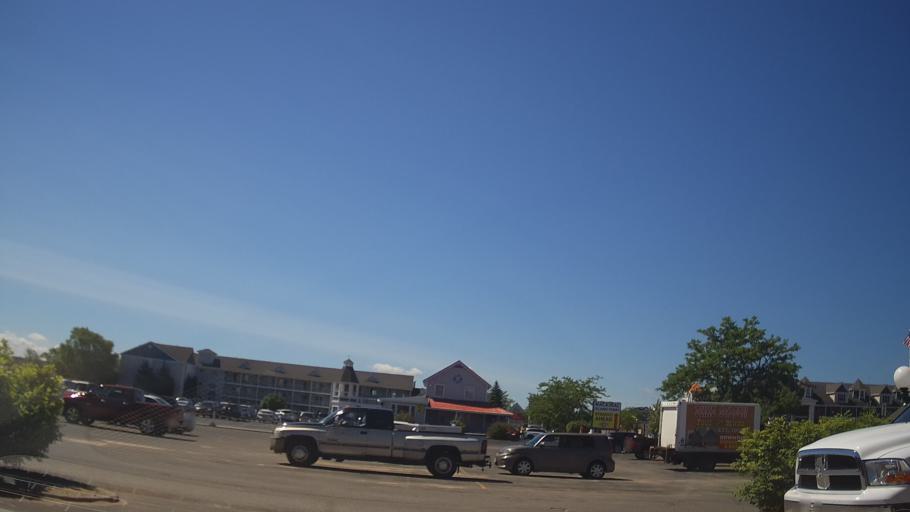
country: US
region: Michigan
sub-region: Mackinac County
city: Saint Ignace
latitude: 45.7746
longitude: -84.7263
